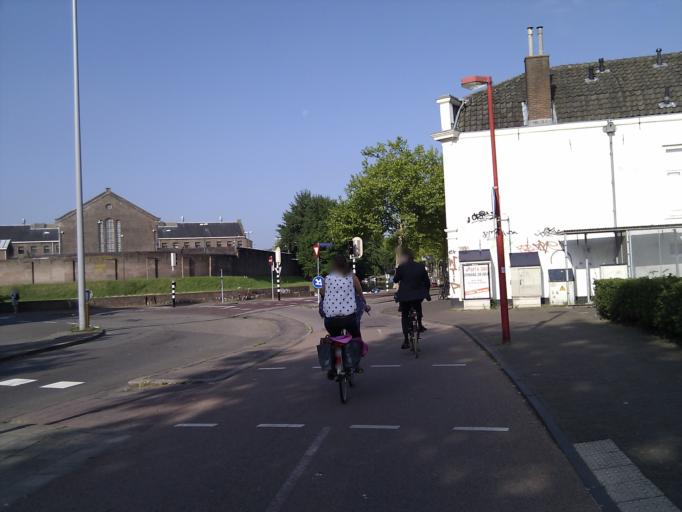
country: NL
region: Utrecht
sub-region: Gemeente Utrecht
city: Utrecht
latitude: 52.0981
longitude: 5.1276
